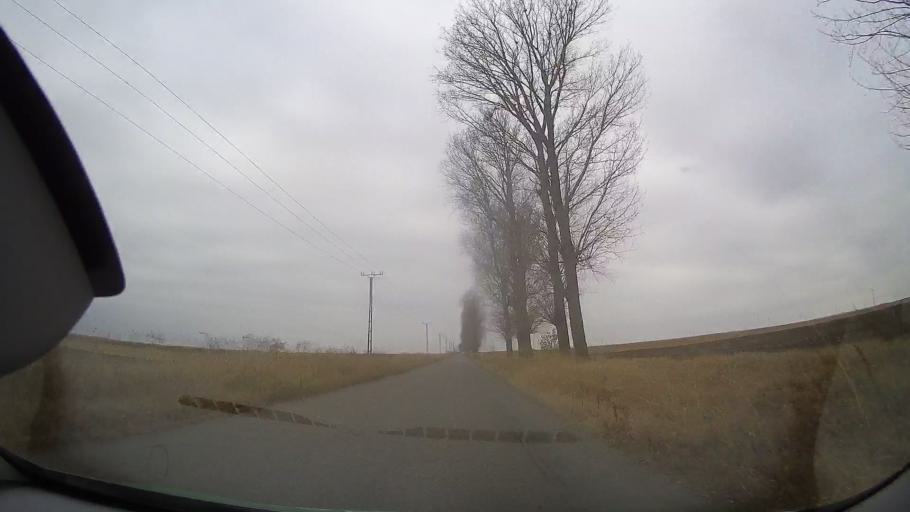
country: RO
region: Buzau
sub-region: Comuna Pogoanele
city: Pogoanele
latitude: 44.9518
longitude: 27.0154
